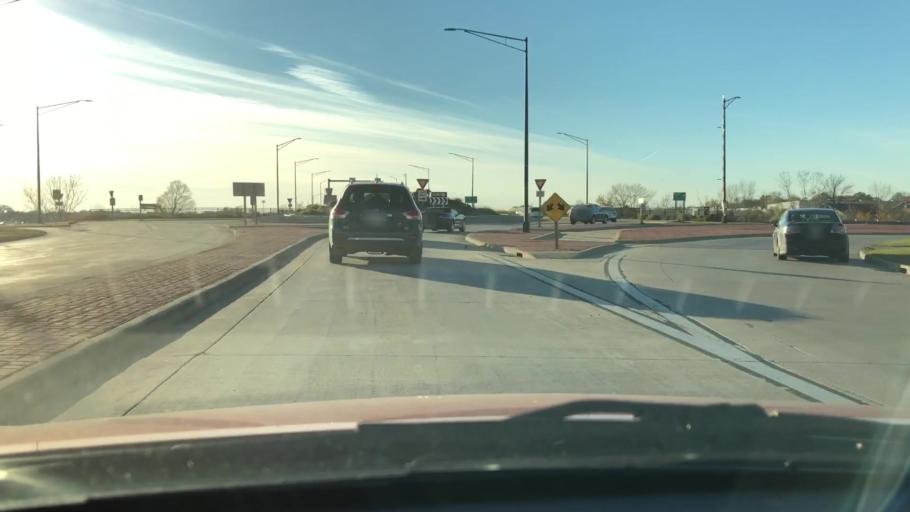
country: US
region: Wisconsin
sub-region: Brown County
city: De Pere
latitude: 44.4308
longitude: -88.1089
